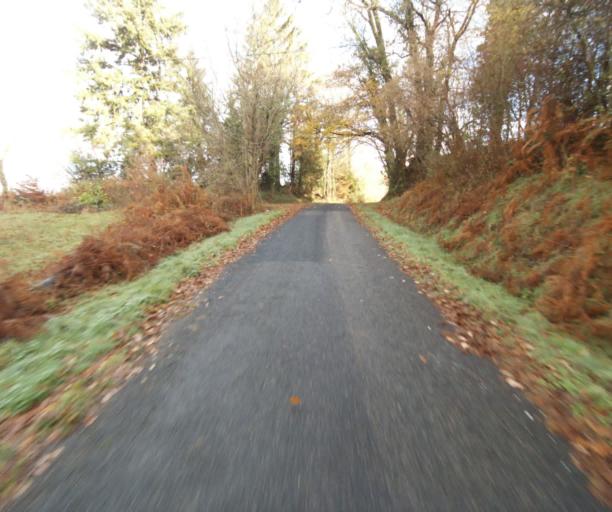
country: FR
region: Limousin
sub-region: Departement de la Correze
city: Saint-Mexant
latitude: 45.2593
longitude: 1.6262
